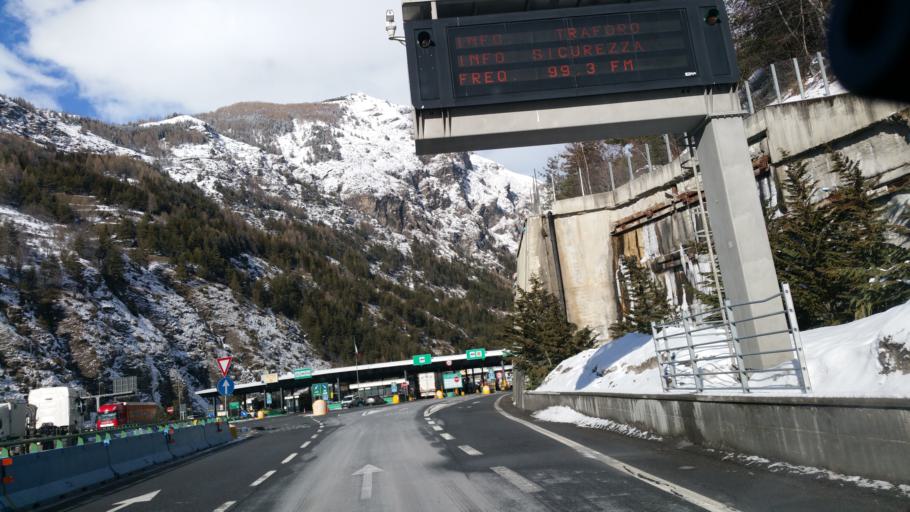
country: IT
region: Piedmont
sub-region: Provincia di Torino
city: Bardonecchia
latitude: 45.0824
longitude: 6.7116
